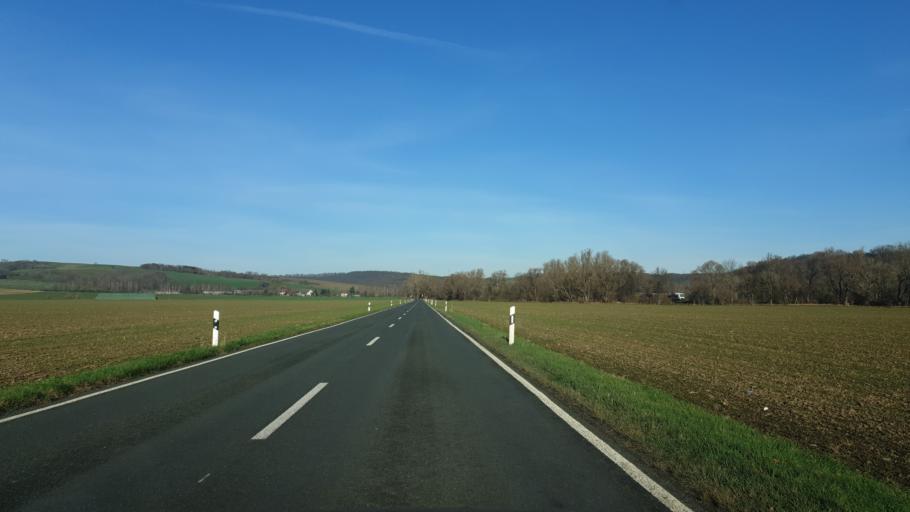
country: DE
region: Thuringia
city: Hartmannsdorf
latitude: 50.9869
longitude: 11.9881
